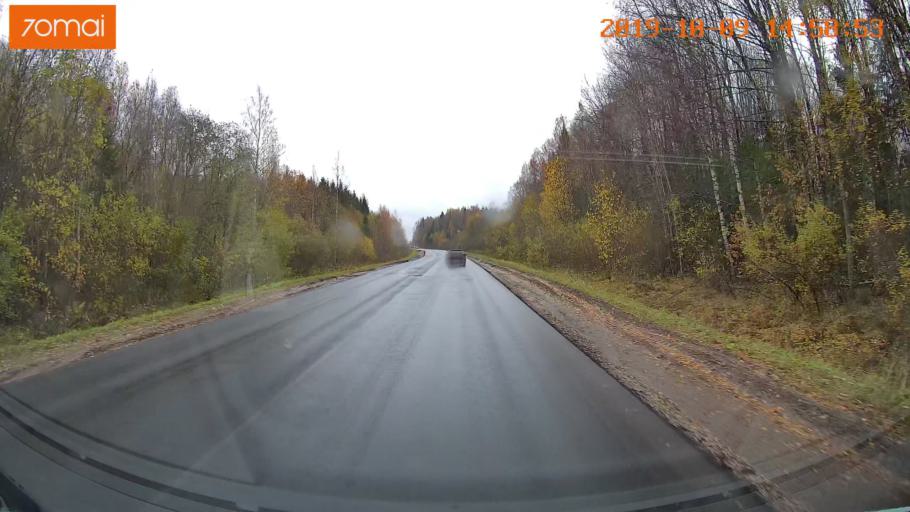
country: RU
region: Kostroma
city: Chistyye Bory
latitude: 58.3233
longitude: 41.6591
